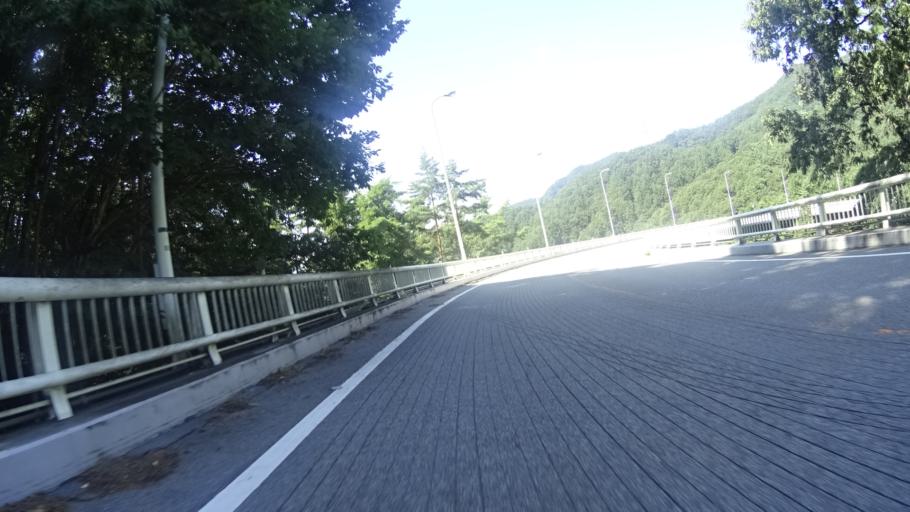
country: JP
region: Yamanashi
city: Enzan
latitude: 35.7502
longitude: 138.8100
